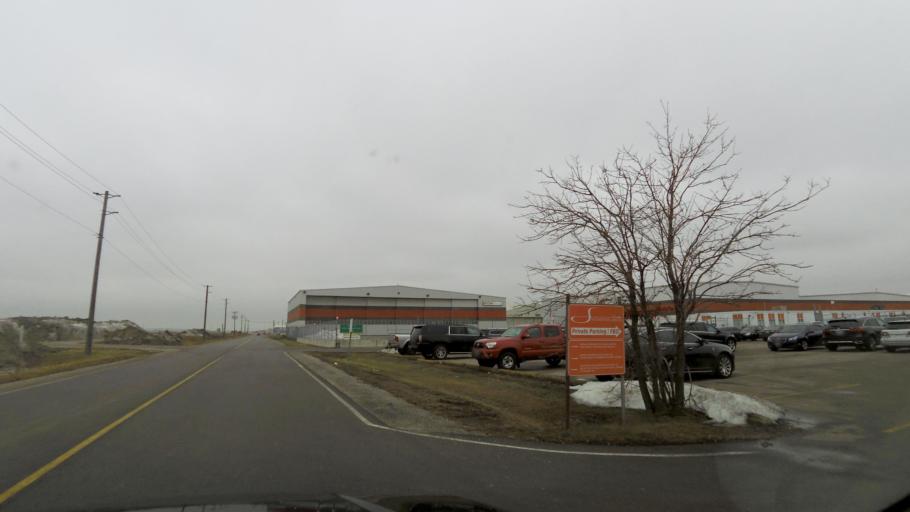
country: CA
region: Ontario
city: Etobicoke
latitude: 43.6948
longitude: -79.6508
